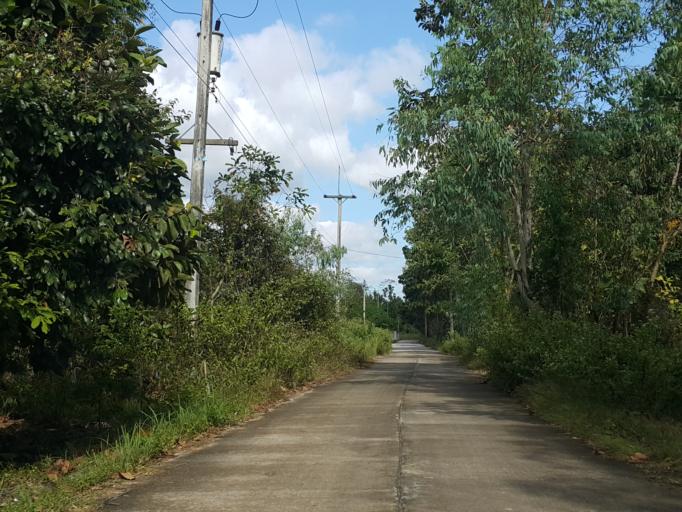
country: TH
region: Lampang
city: Hang Chat
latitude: 18.3456
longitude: 99.3626
